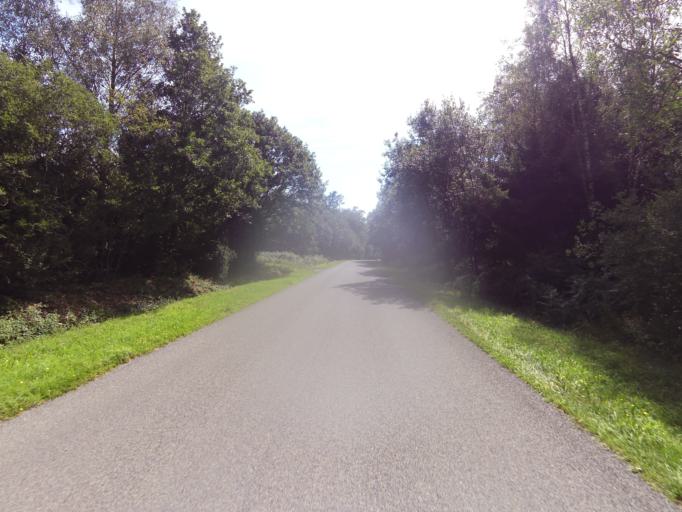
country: BE
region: Wallonia
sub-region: Province du Luxembourg
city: Saint-Hubert
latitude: 50.0494
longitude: 5.3492
